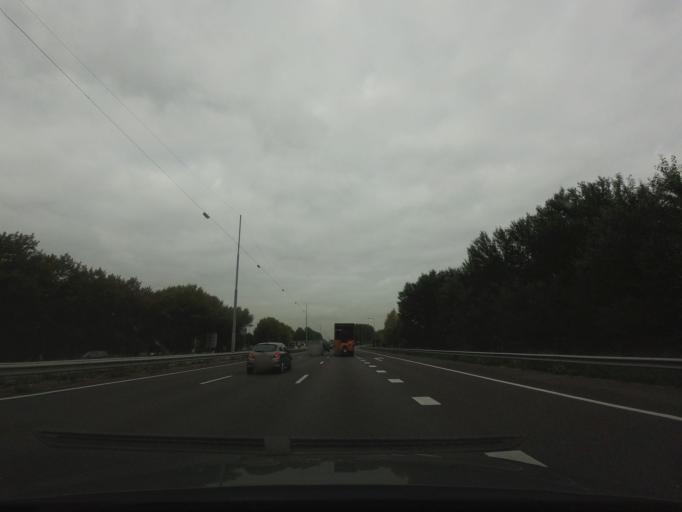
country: NL
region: North Holland
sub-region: Gemeente Diemen
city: Diemen
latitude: 52.3862
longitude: 4.9701
